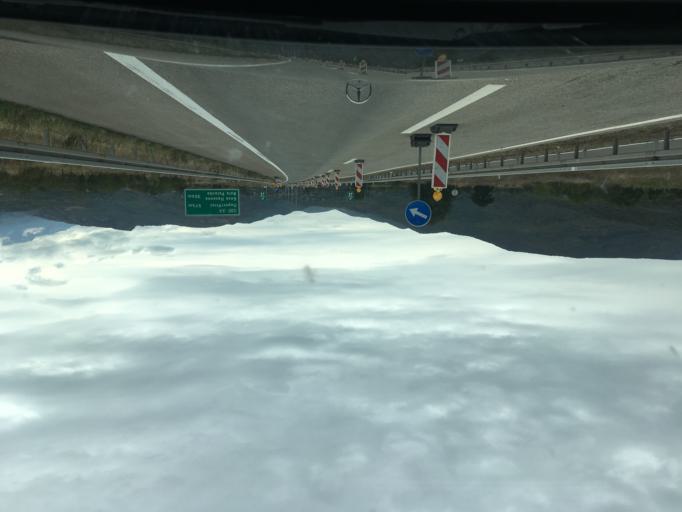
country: RS
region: Central Serbia
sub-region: Nisavski Okrug
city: Niska Banja
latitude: 43.3161
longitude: 22.0228
